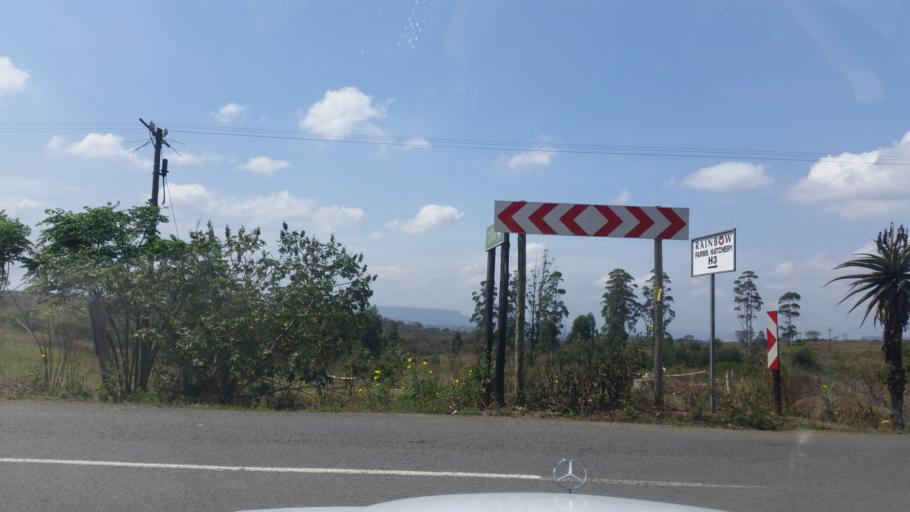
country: ZA
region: KwaZulu-Natal
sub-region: uMgungundlovu District Municipality
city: Camperdown
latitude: -29.7024
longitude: 30.4925
